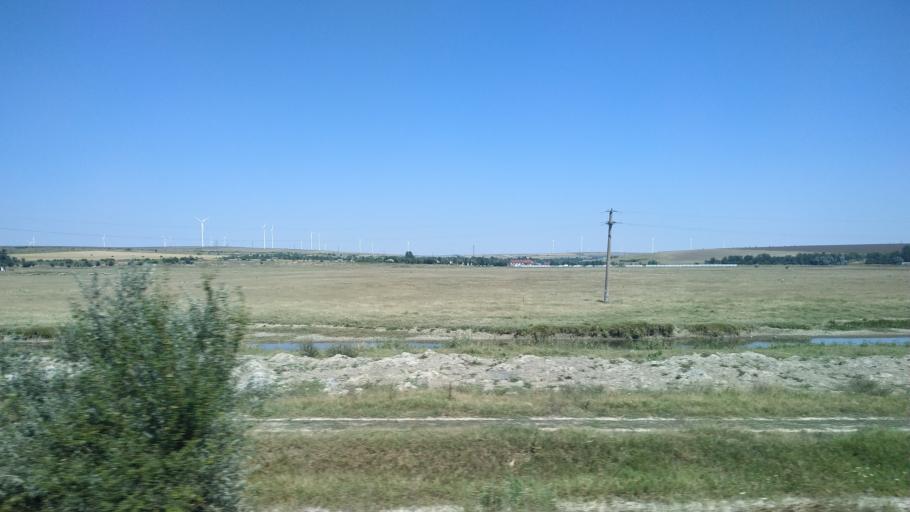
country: RO
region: Constanta
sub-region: Comuna Mircea Voda
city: Mircea Voda
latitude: 44.2639
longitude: 28.1701
